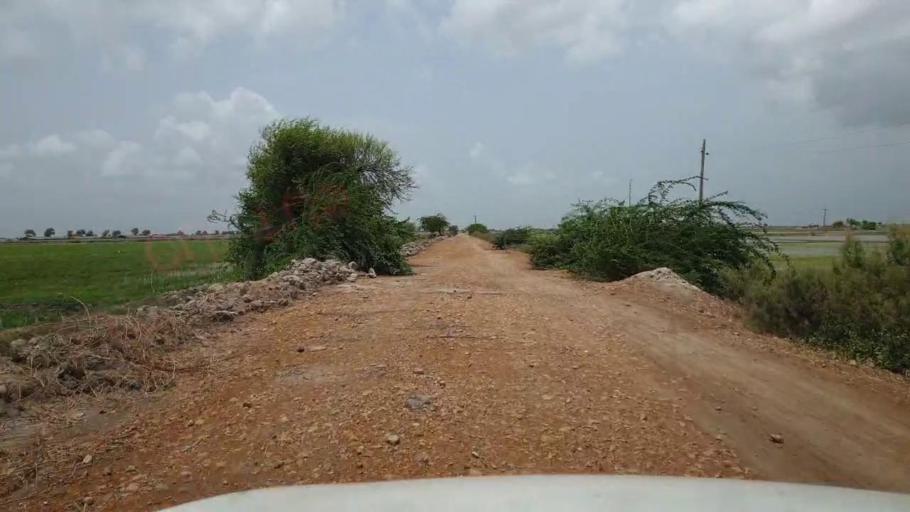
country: PK
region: Sindh
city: Kario
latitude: 24.7623
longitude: 68.4576
